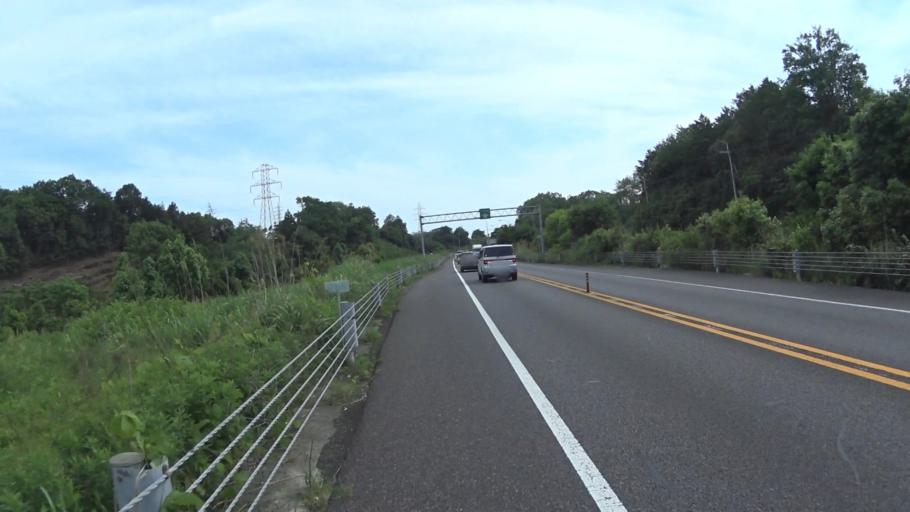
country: JP
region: Shiga Prefecture
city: Kitahama
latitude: 35.0956
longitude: 135.8905
